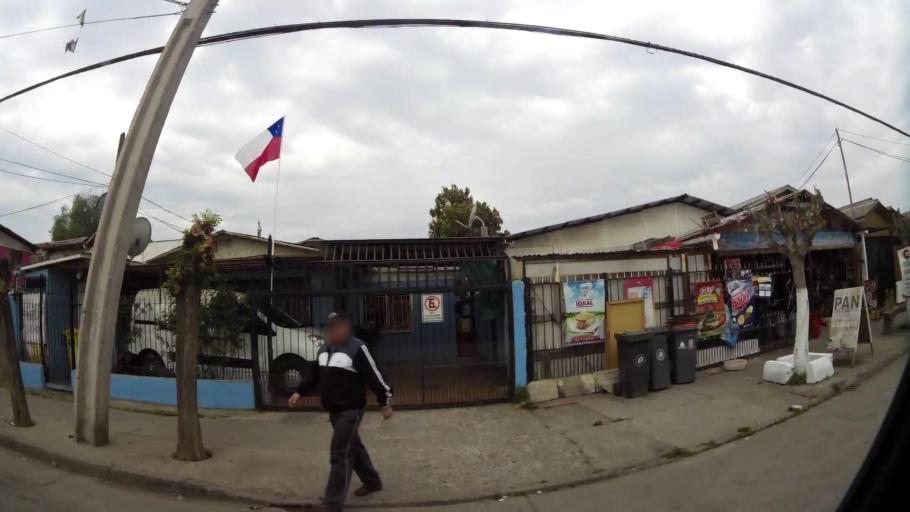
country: CL
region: Santiago Metropolitan
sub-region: Provincia de Santiago
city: Lo Prado
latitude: -33.4955
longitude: -70.7623
